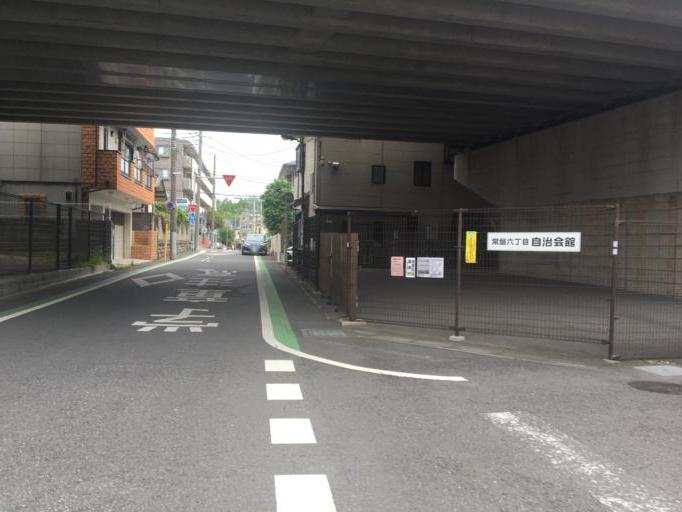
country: JP
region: Saitama
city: Yono
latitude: 35.8605
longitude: 139.6413
